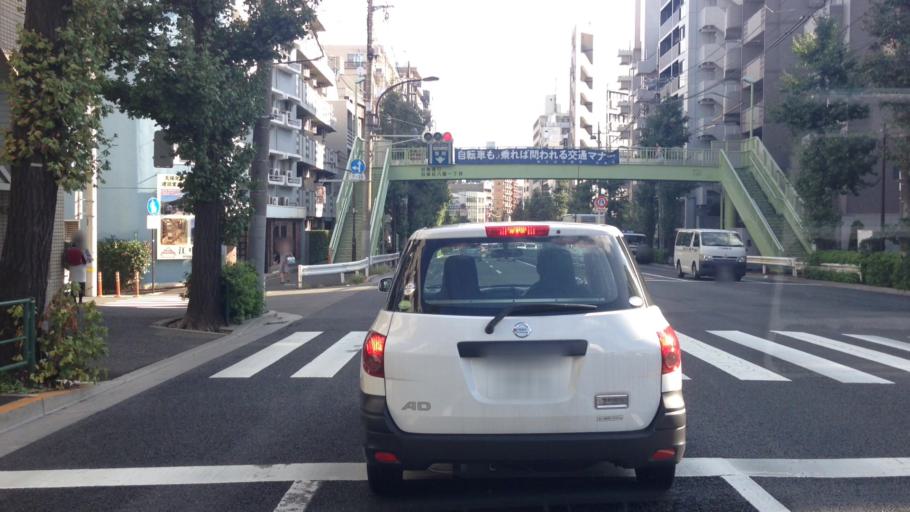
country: JP
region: Tokyo
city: Tokyo
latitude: 35.6163
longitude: 139.6722
